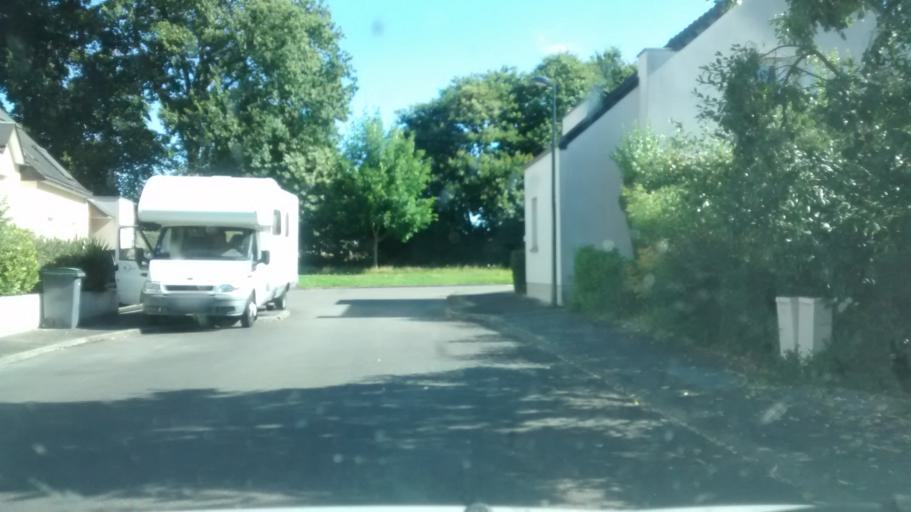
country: FR
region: Brittany
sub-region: Departement d'Ille-et-Vilaine
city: Chantepie
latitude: 48.0951
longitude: -1.6158
